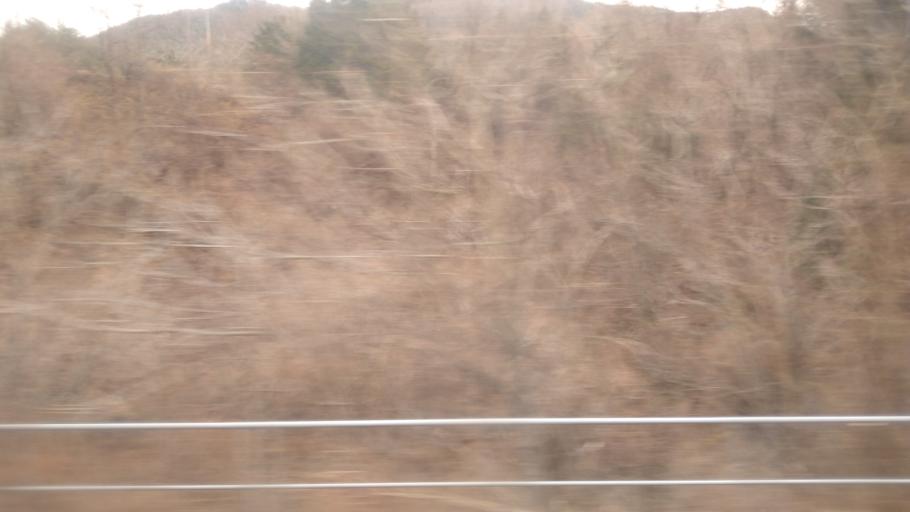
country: JP
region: Nagano
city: Ina
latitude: 35.9425
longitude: 137.7841
